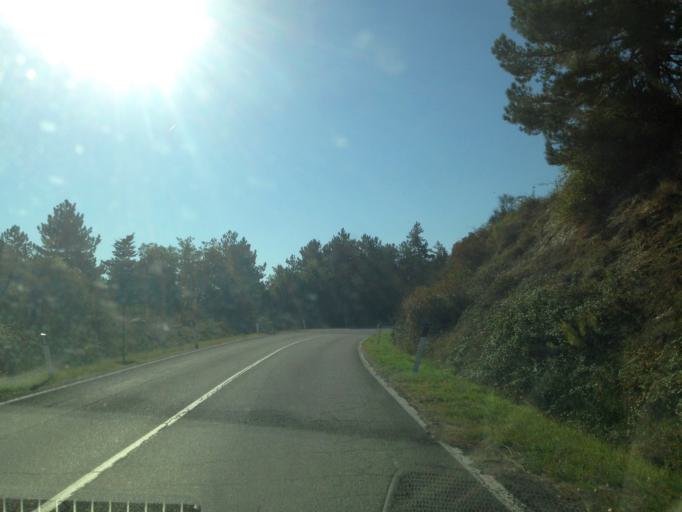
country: IT
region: Tuscany
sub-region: Provincia di Siena
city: Castellina in Chianti
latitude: 43.4543
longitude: 11.2922
